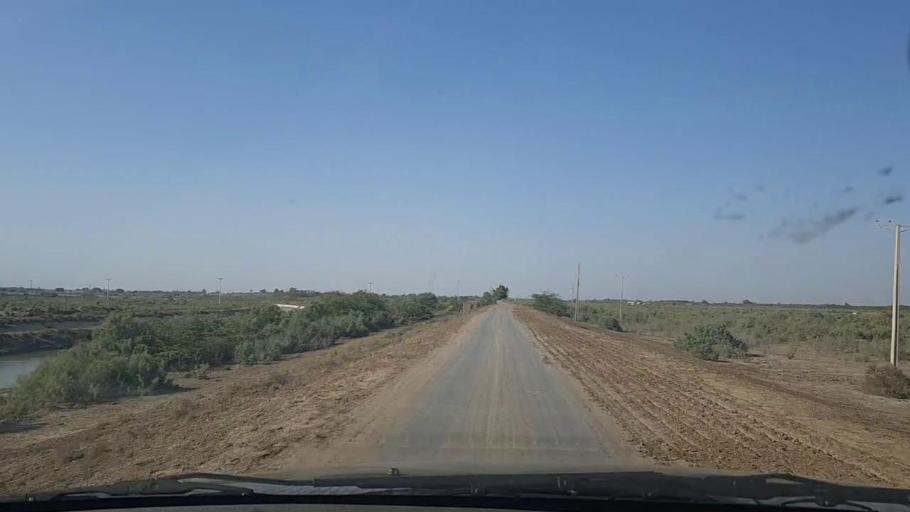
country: PK
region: Sindh
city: Chuhar Jamali
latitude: 24.3097
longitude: 67.7548
